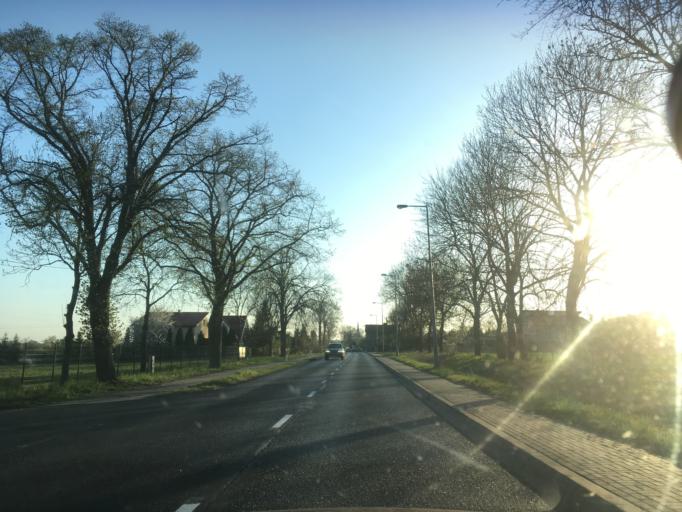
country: PL
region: Lubusz
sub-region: Powiat gorzowski
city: Jenin
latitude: 52.6986
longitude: 15.1079
